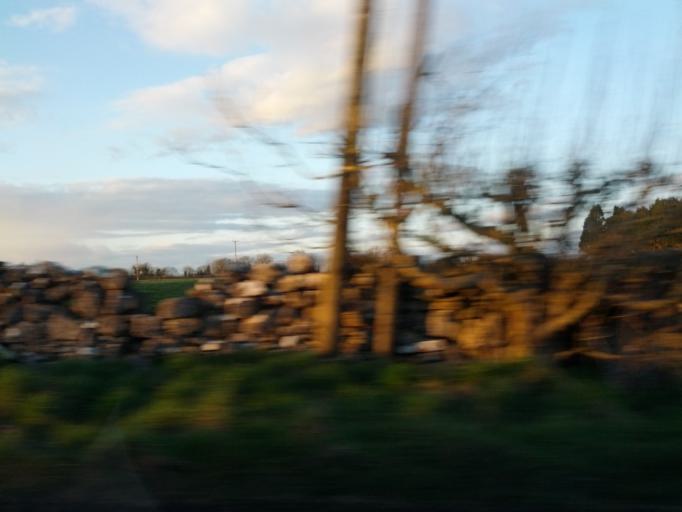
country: IE
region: Connaught
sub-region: County Galway
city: Athenry
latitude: 53.2722
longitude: -8.6675
